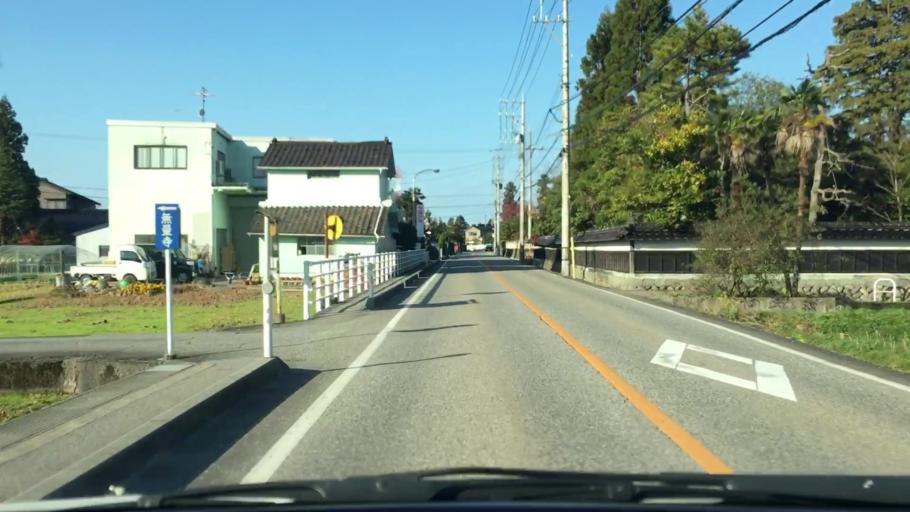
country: JP
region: Toyama
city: Kamiichi
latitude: 36.7070
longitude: 137.3057
